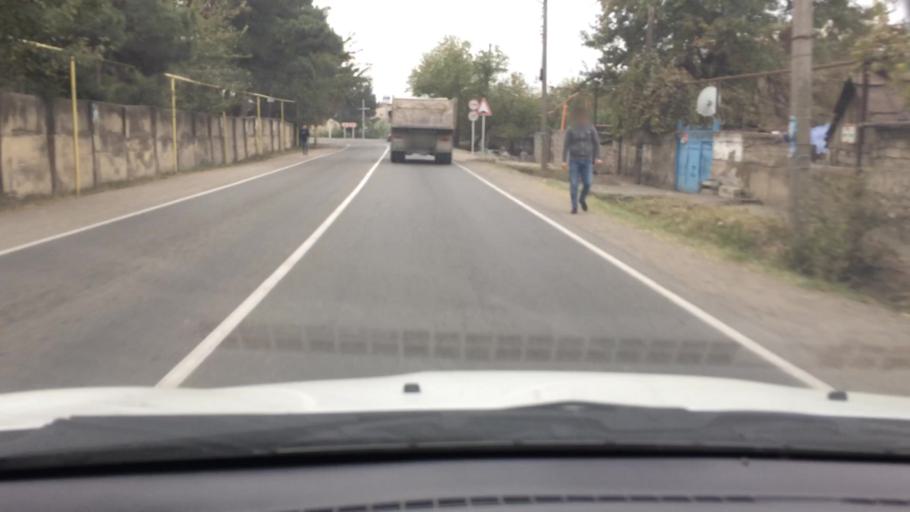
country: GE
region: Kvemo Kartli
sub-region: Marneuli
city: Marneuli
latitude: 41.4783
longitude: 44.7987
